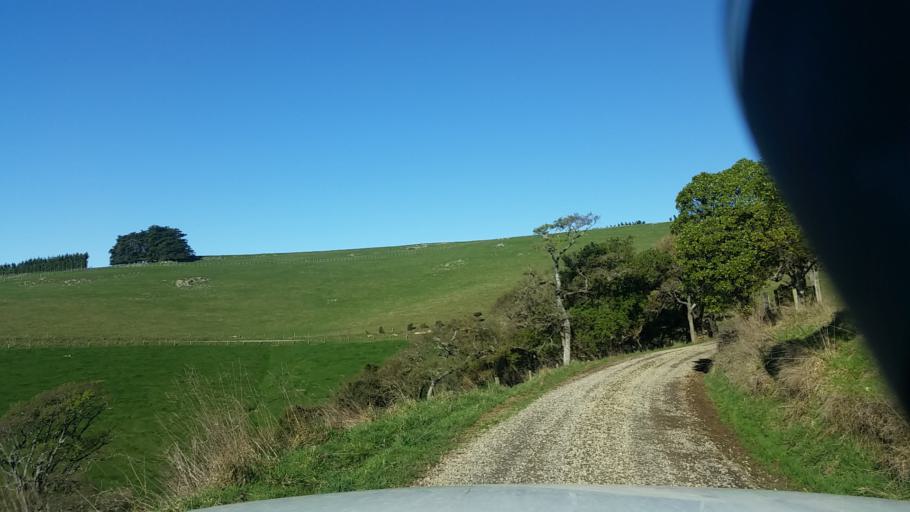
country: NZ
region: Canterbury
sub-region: Christchurch City
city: Christchurch
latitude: -43.6538
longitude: 172.9748
